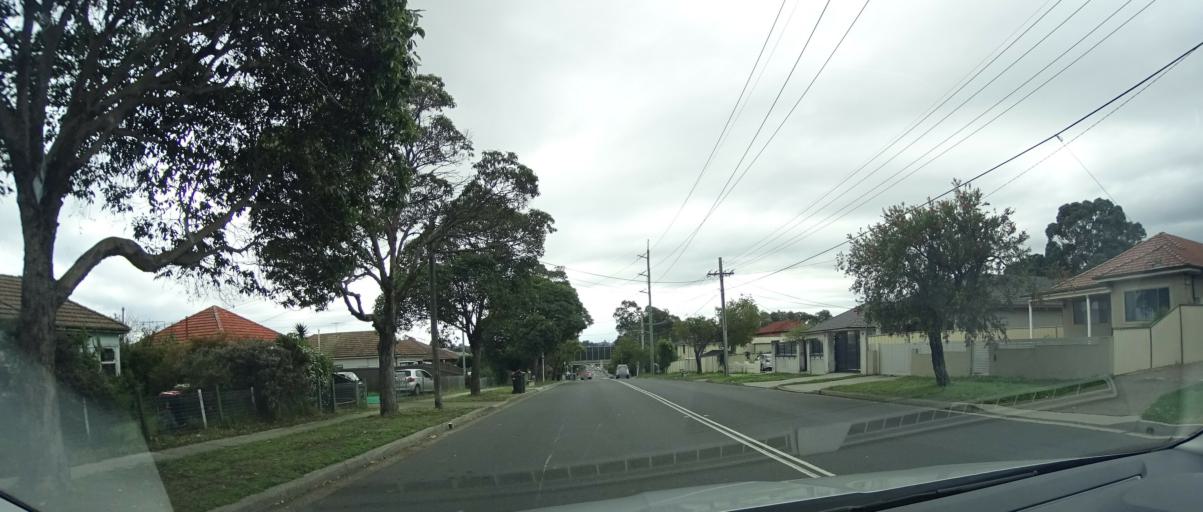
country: AU
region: New South Wales
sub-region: Bankstown
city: Revesby
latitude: -33.9415
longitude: 151.0106
